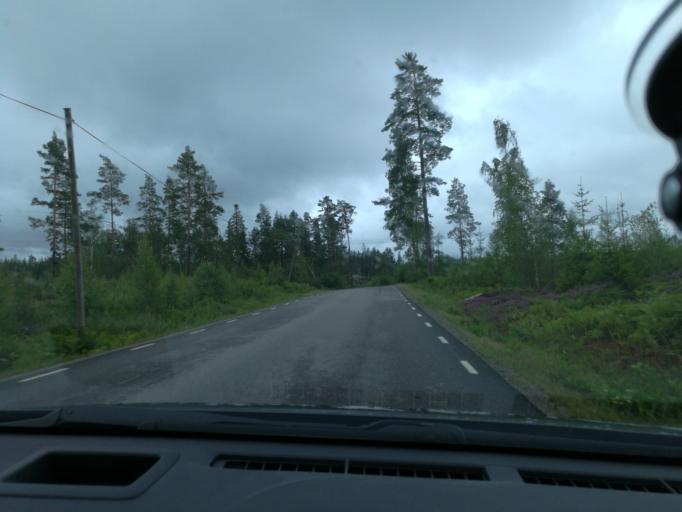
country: SE
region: OEstergoetland
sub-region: Norrkopings Kommun
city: Jursla
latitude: 58.8024
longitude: 16.1337
